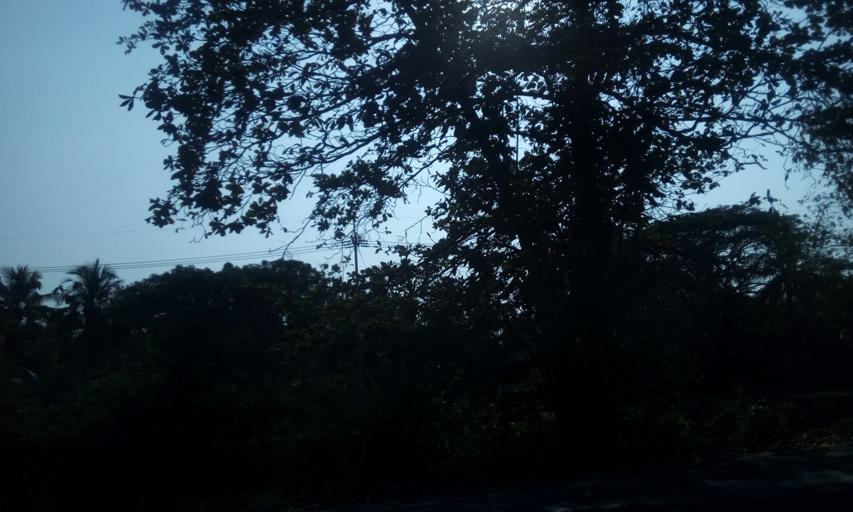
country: TH
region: Sing Buri
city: Phrom Buri
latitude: 14.7524
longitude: 100.4388
